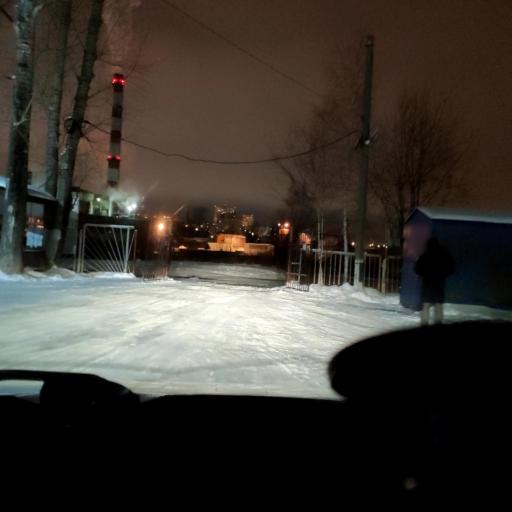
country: RU
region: Perm
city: Perm
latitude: 57.9971
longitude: 56.3205
